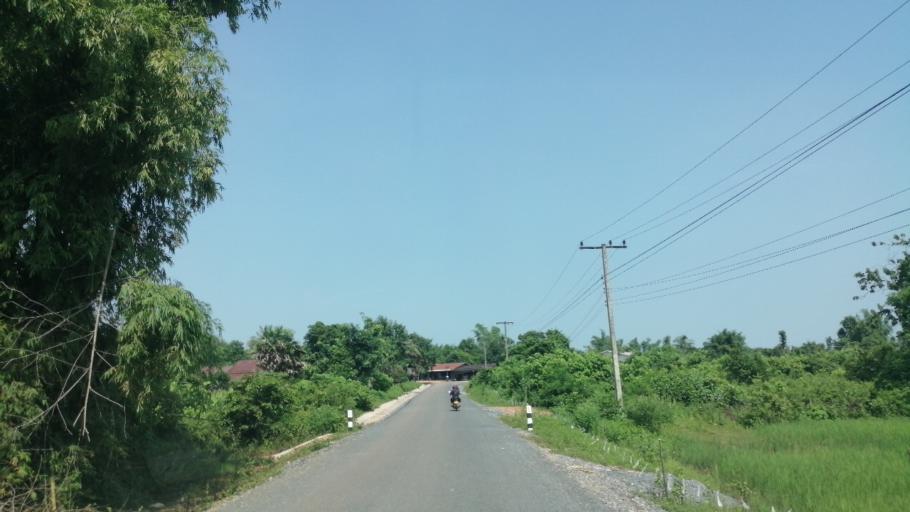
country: LA
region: Bolikhamxai
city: Bolikhan
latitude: 18.4604
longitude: 103.7971
